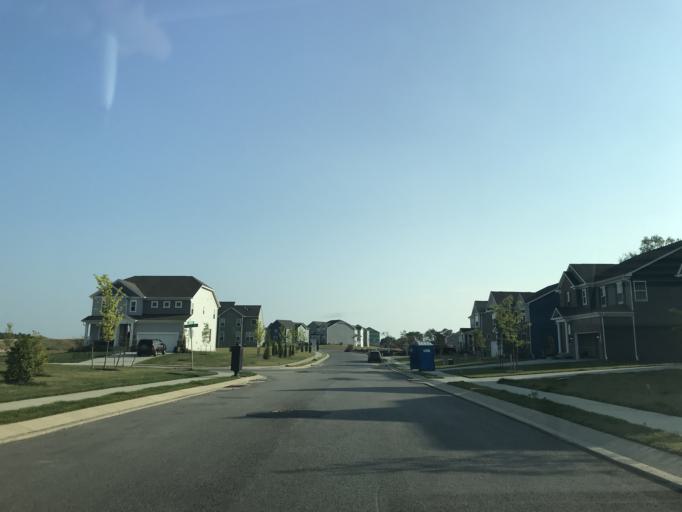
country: US
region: Maryland
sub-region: Carroll County
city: Westminster
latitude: 39.5582
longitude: -76.9744
